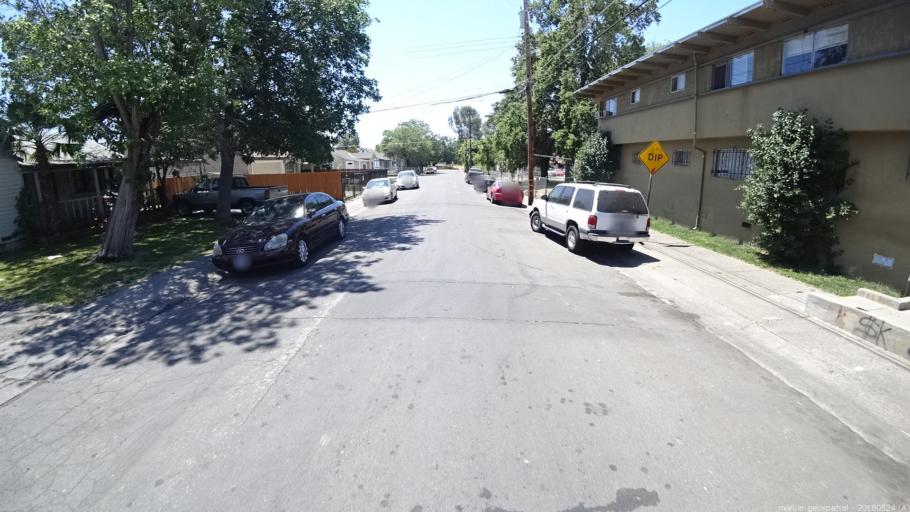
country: US
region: California
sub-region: Sacramento County
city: Sacramento
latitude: 38.6154
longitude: -121.4524
